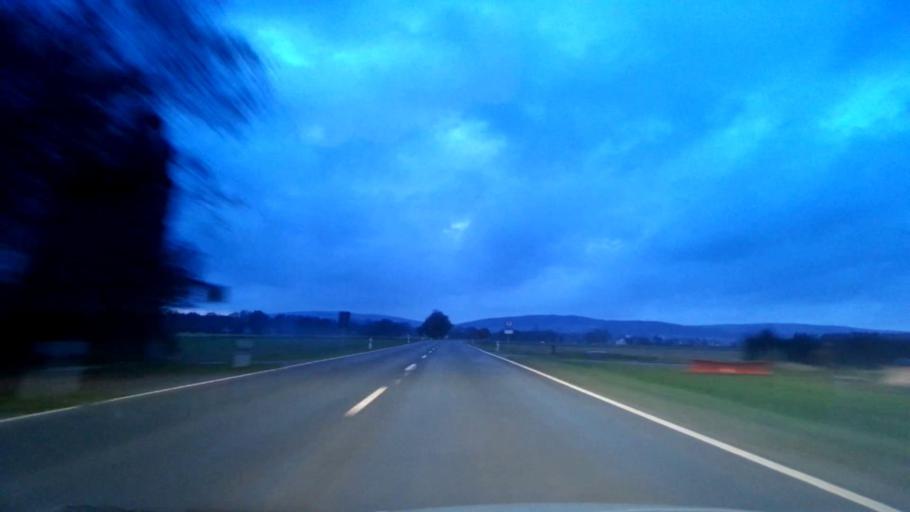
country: DE
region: Bavaria
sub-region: Upper Palatinate
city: Immenreuth
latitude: 49.8942
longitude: 11.8764
